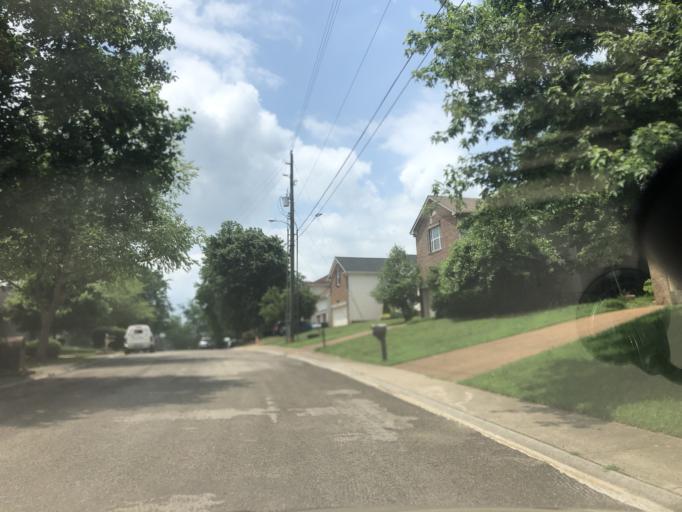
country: US
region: Tennessee
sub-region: Davidson County
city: Lakewood
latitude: 36.2165
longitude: -86.6315
